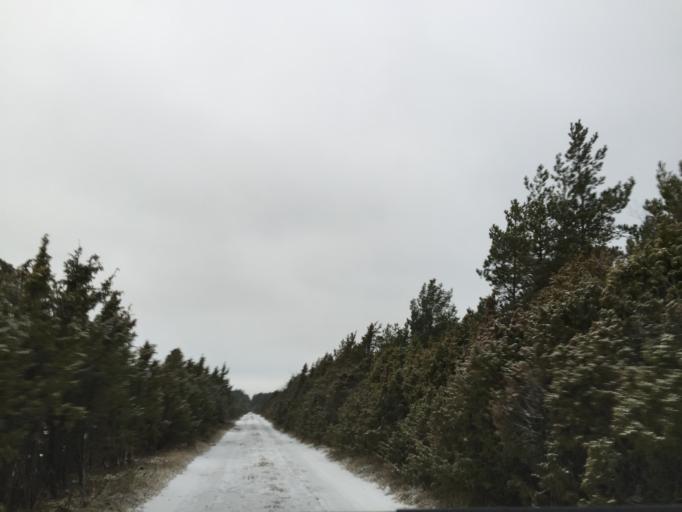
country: EE
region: Saare
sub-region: Orissaare vald
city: Orissaare
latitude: 58.5466
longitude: 23.3842
